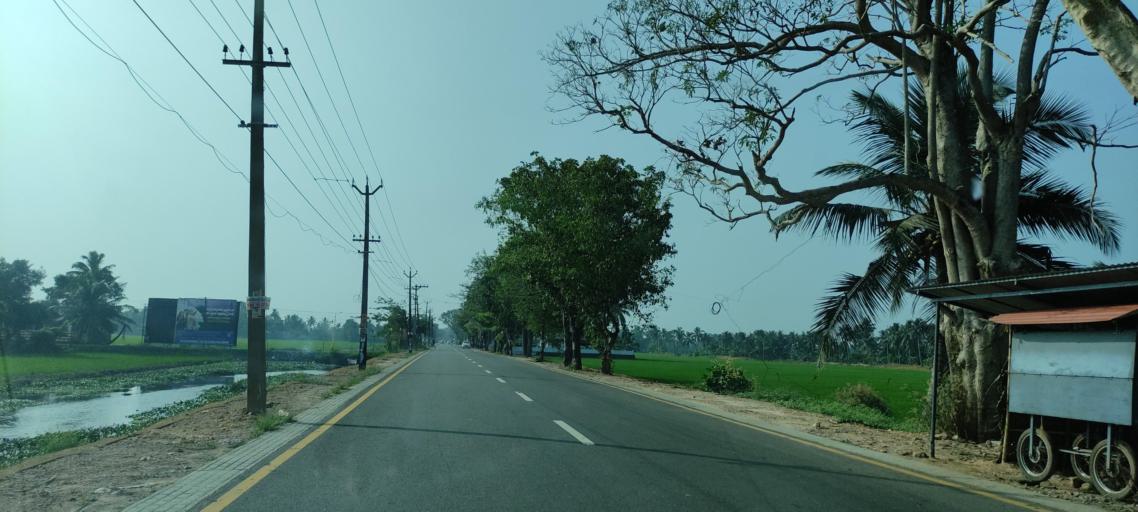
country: IN
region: Kerala
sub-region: Kottayam
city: Changanacheri
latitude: 9.3665
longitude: 76.4359
